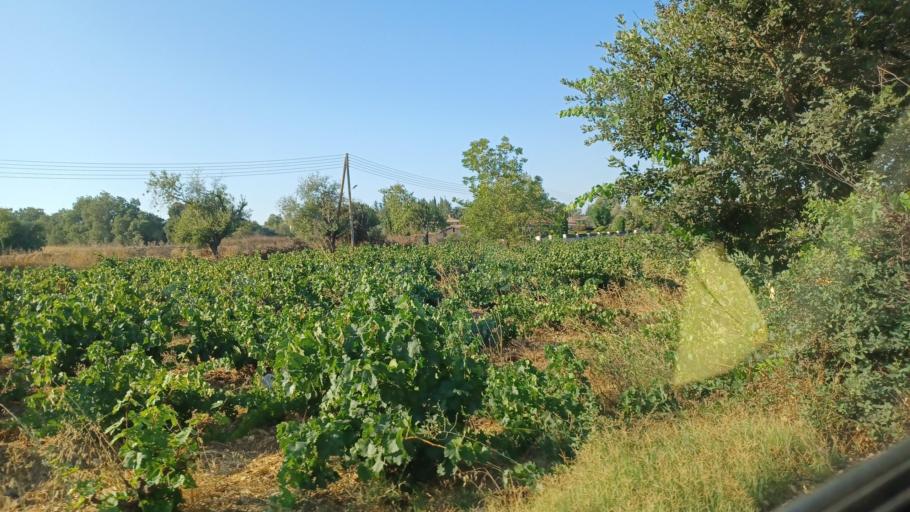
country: CY
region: Pafos
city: Mesogi
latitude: 34.8921
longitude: 32.5119
